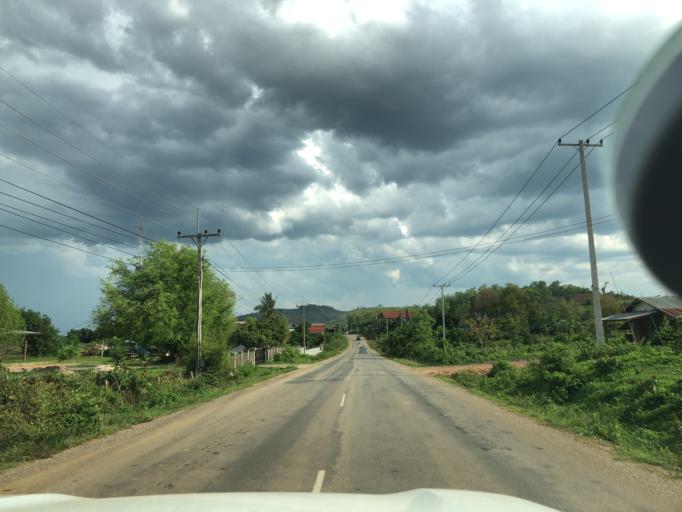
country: TH
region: Uttaradit
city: Ban Khok
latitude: 18.1506
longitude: 101.3824
